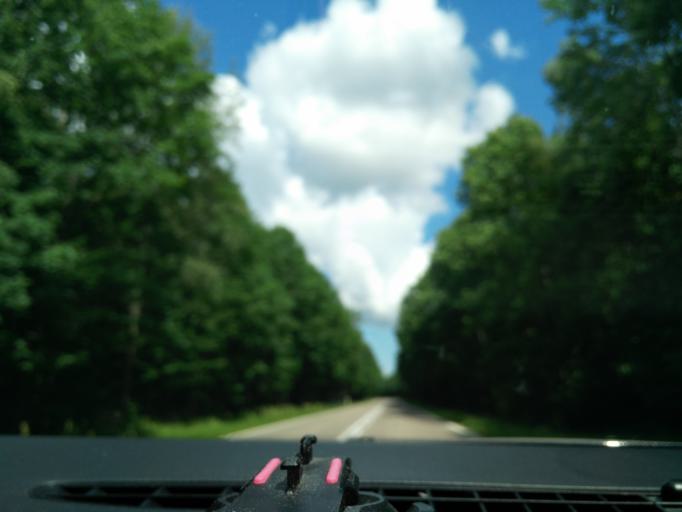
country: PL
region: Podlasie
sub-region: Powiat siemiatycki
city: Dziadkowice
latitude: 52.5406
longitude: 22.9132
